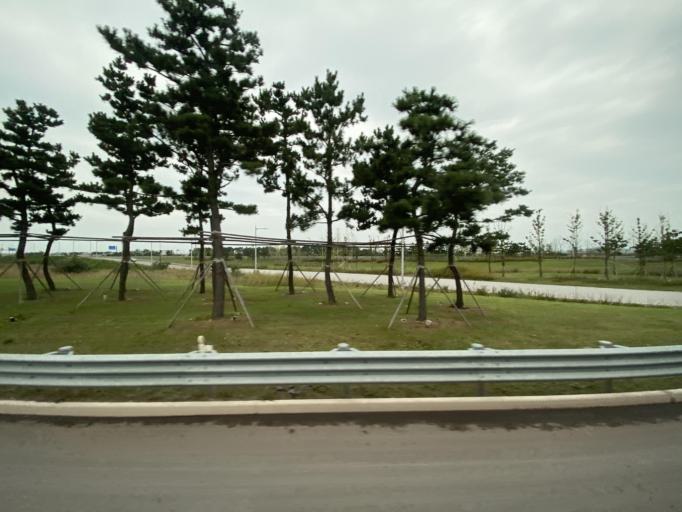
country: KR
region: Incheon
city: Seonwon
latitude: 37.4928
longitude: 126.4179
